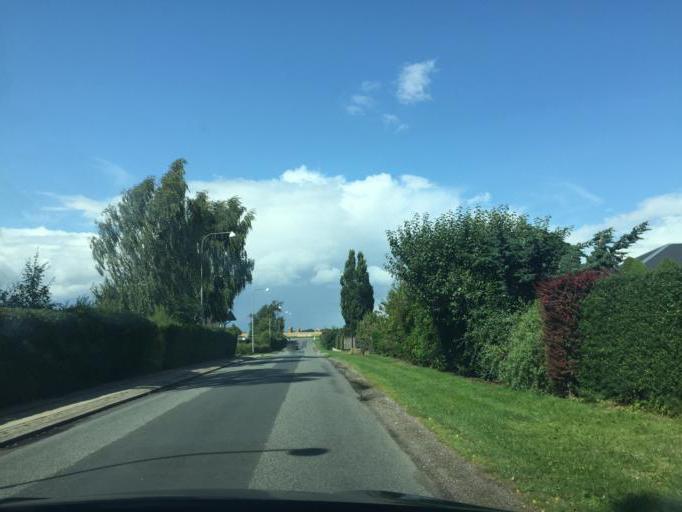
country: DK
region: South Denmark
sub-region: Faaborg-Midtfyn Kommune
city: Arslev
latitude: 55.3119
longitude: 10.4872
